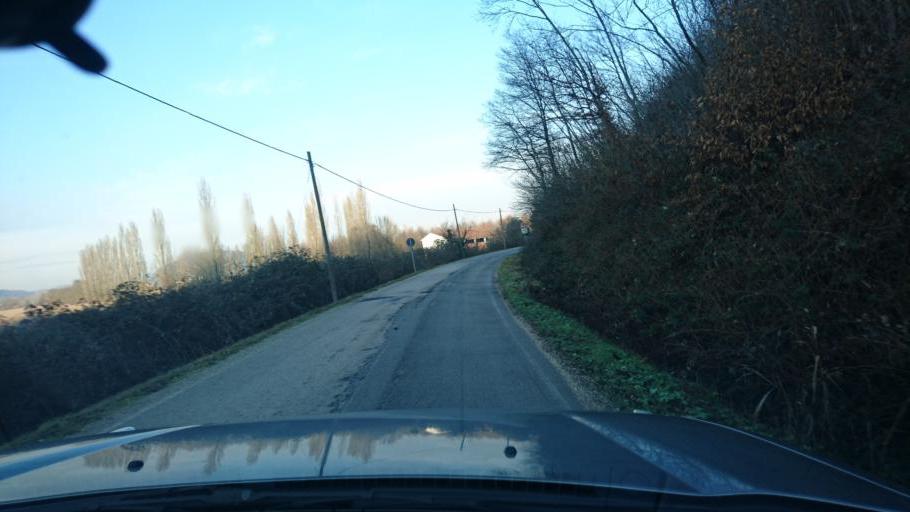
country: IT
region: Veneto
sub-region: Provincia di Padova
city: Torreglia
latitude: 45.3205
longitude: 11.7456
